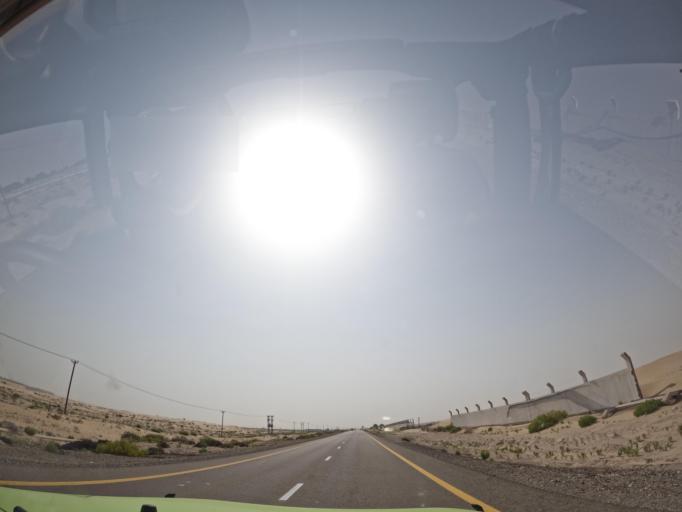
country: AE
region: Dubai
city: Dubai
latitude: 24.6689
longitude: 55.1704
